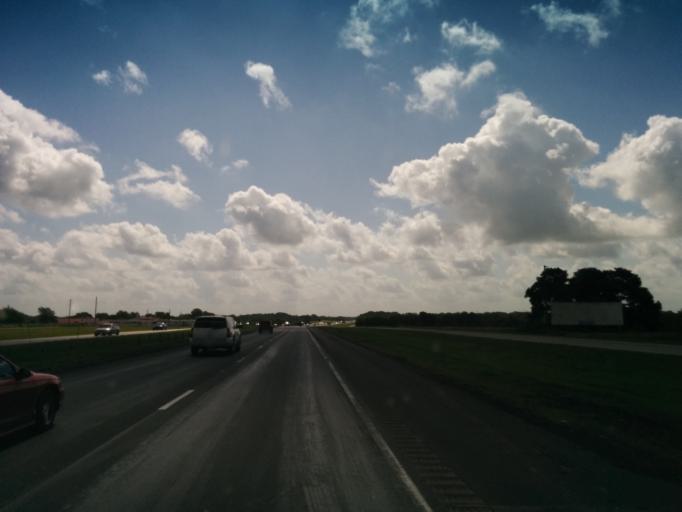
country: US
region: Texas
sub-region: Colorado County
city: Weimar
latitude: 29.6922
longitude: -96.7387
